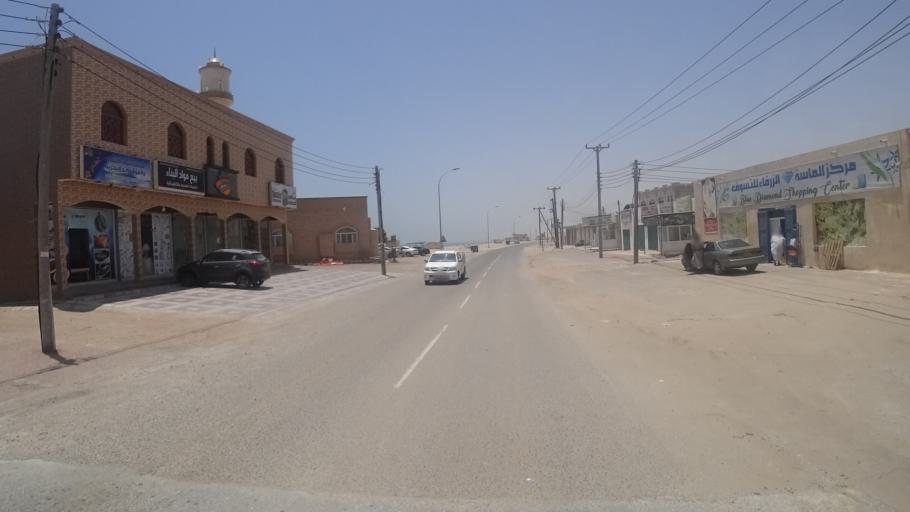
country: OM
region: Ash Sharqiyah
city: Sur
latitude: 22.0824
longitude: 59.6849
